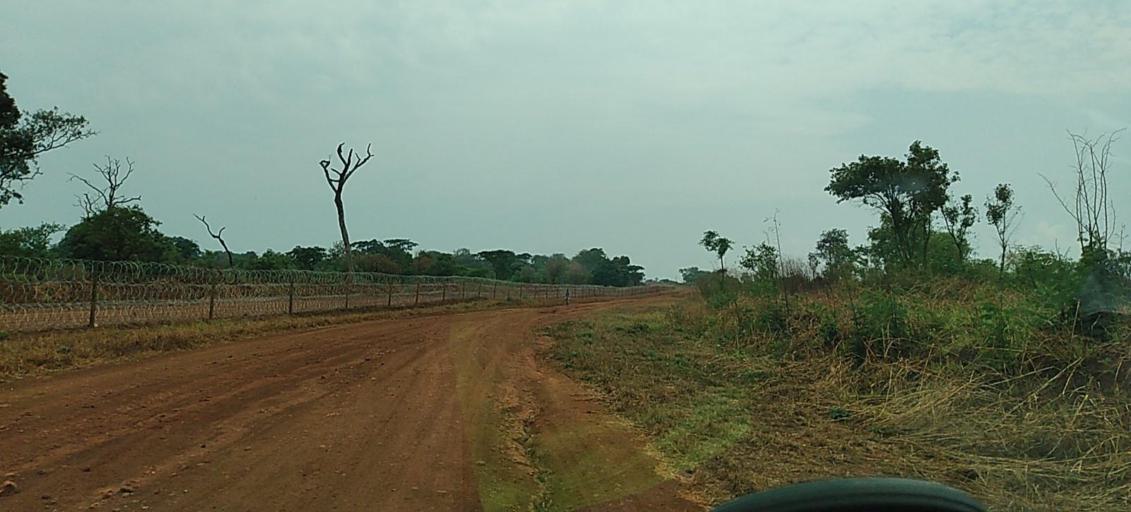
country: ZM
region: North-Western
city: Kansanshi
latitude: -12.1006
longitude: 26.4910
